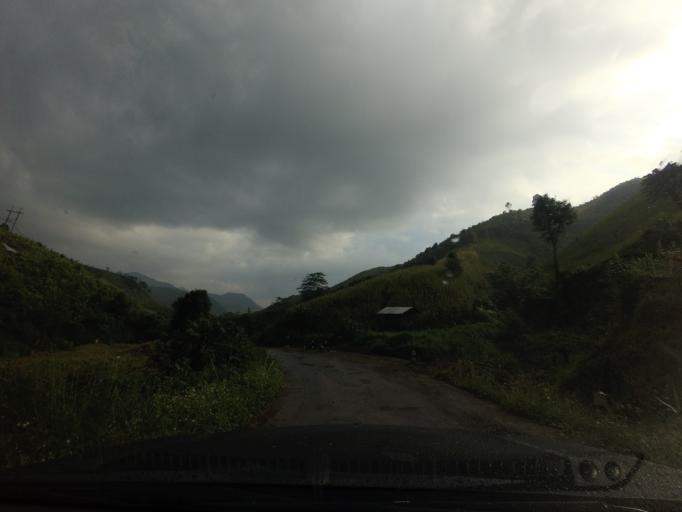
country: TH
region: Nan
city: Bo Kluea
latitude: 19.2978
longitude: 101.1739
